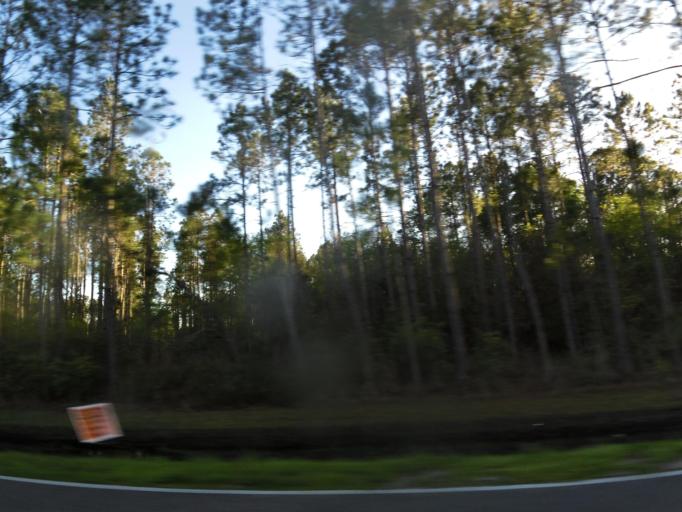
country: US
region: Florida
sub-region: Bradford County
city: Starke
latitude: 29.8558
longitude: -82.1053
